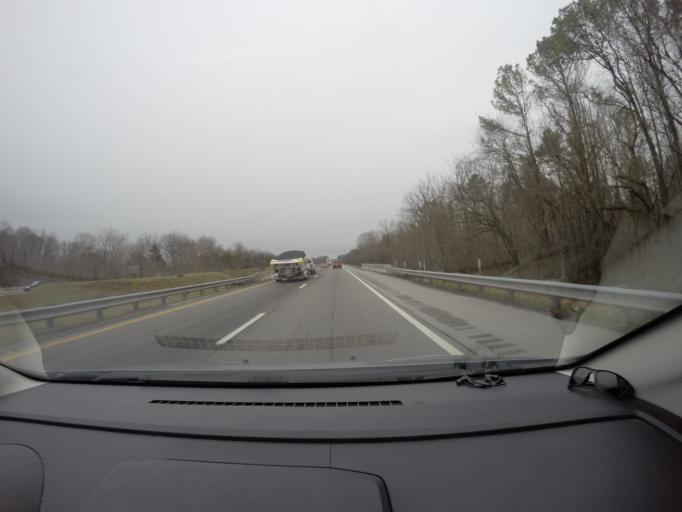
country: US
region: Tennessee
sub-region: Coffee County
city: Manchester
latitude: 35.3795
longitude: -85.9783
